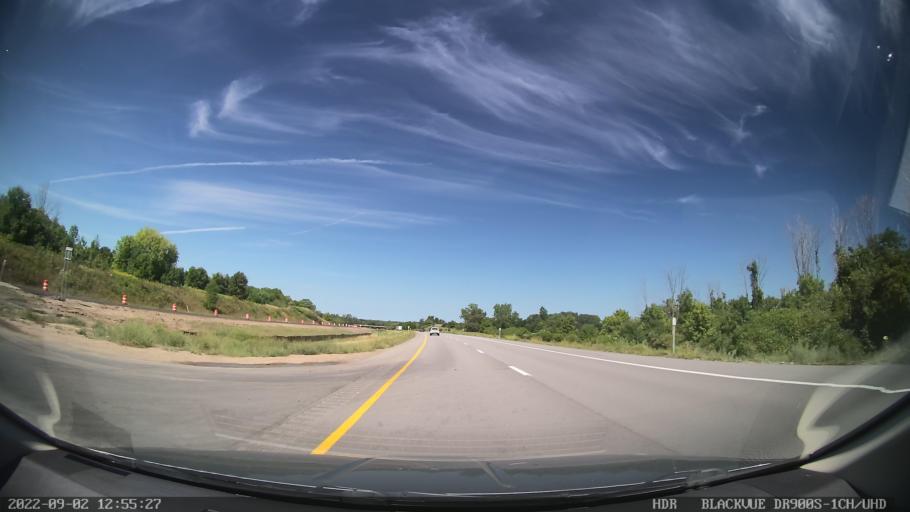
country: US
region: New York
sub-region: Livingston County
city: Avon
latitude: 42.9410
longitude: -77.6917
